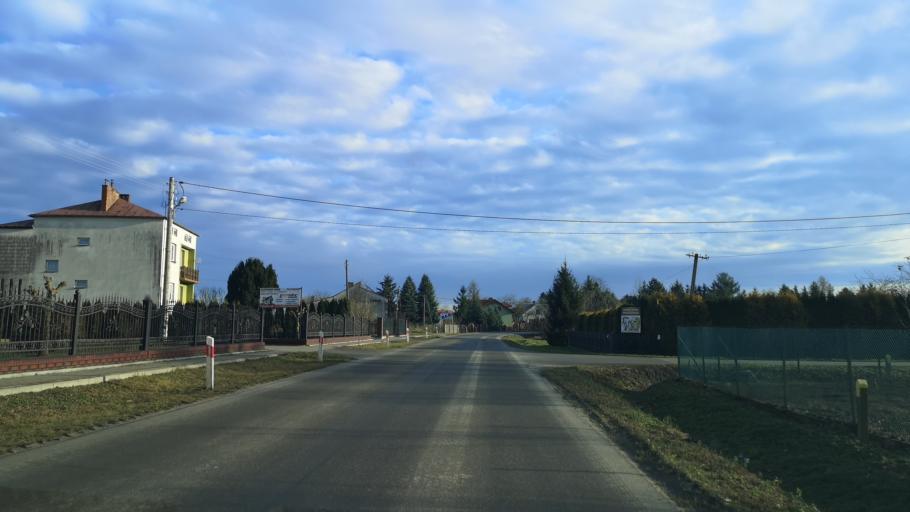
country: PL
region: Subcarpathian Voivodeship
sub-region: Powiat lezajski
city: Piskorowice
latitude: 50.2424
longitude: 22.5161
